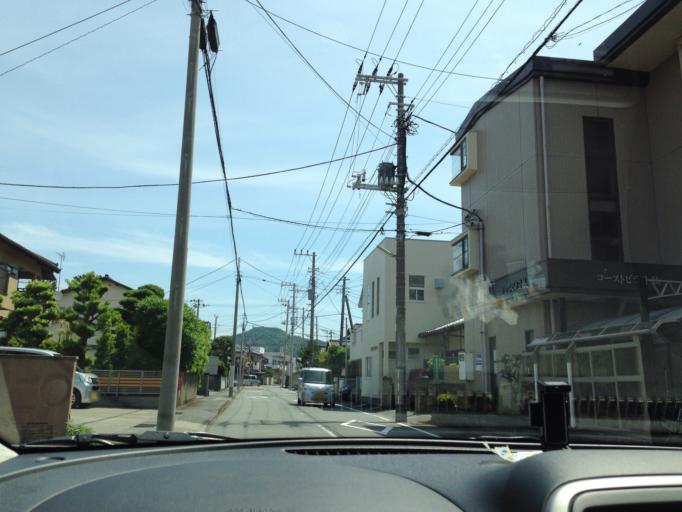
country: JP
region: Shizuoka
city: Numazu
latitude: 35.0768
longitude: 138.8659
